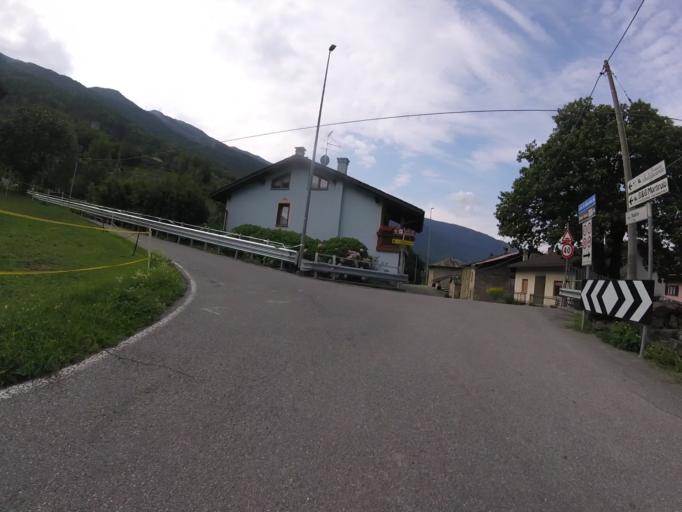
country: IT
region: Lombardy
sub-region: Provincia di Sondrio
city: Mazzo di Valtellina
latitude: 46.2538
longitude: 10.2561
